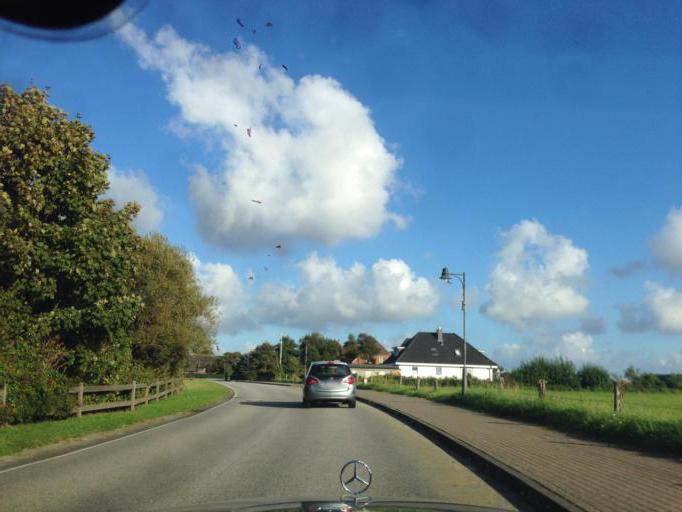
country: DE
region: Schleswig-Holstein
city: Sylt-Ost
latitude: 54.8703
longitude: 8.4358
